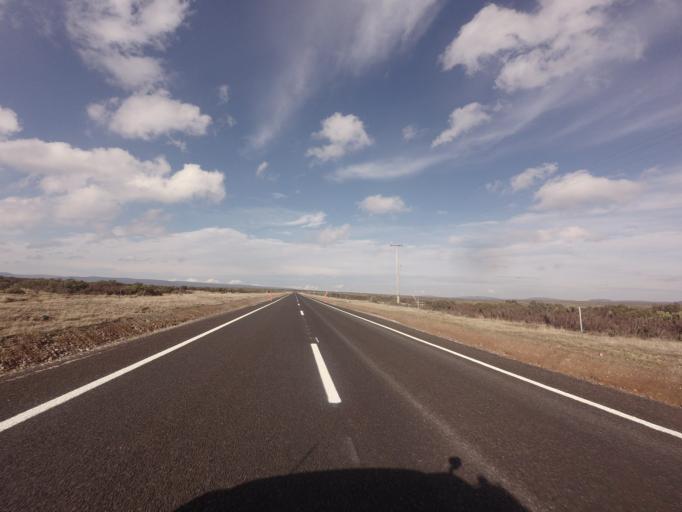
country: AU
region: Tasmania
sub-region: Meander Valley
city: Deloraine
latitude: -41.9099
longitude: 146.6795
